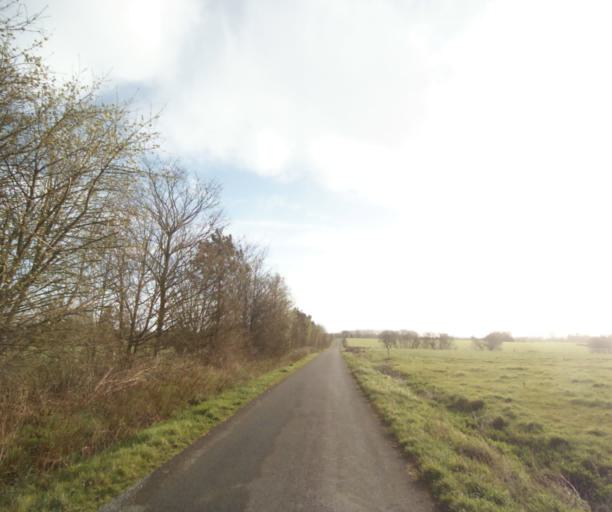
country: FR
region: Pays de la Loire
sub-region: Departement de la Loire-Atlantique
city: Bouvron
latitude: 47.3987
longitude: -1.8782
